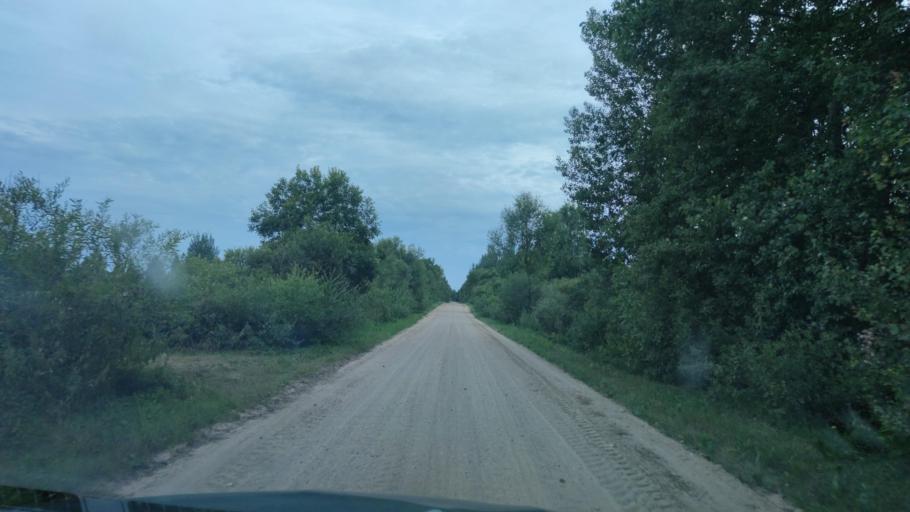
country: BY
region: Vitebsk
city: Pastavy
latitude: 55.1190
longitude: 27.1507
